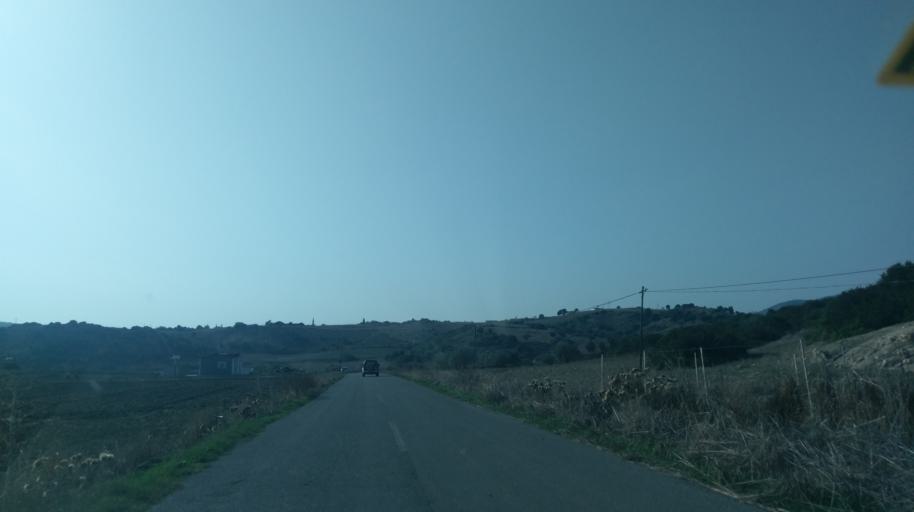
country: CY
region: Ammochostos
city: Rizokarpaso
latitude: 35.5117
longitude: 34.2836
